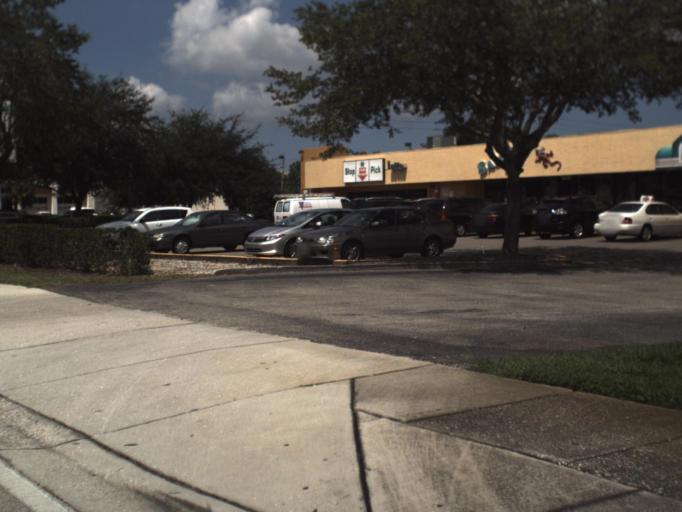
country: US
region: Florida
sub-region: Manatee County
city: South Bradenton
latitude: 27.4626
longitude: -82.6032
